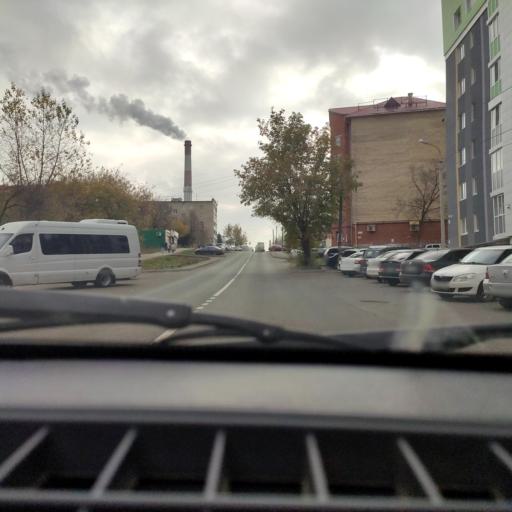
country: RU
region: Bashkortostan
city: Ufa
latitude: 54.7167
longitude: 55.9998
